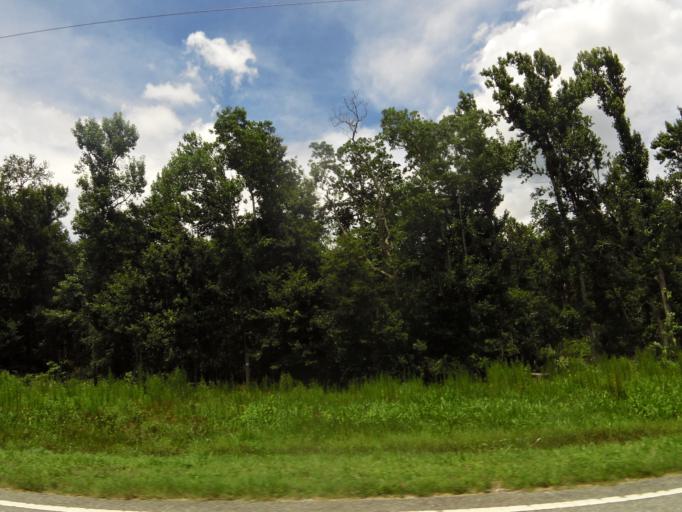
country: US
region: Florida
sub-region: Flagler County
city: Palm Coast
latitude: 29.6586
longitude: -81.2911
